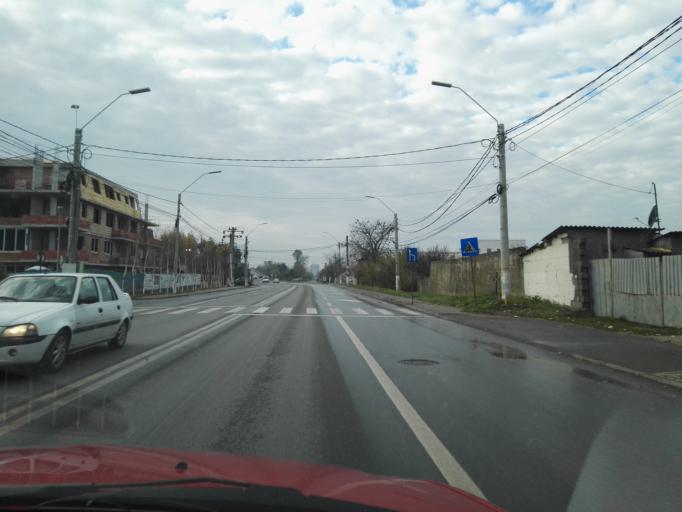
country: RO
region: Ilfov
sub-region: Comuna Magurele
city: Magurele
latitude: 44.3631
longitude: 26.0388
